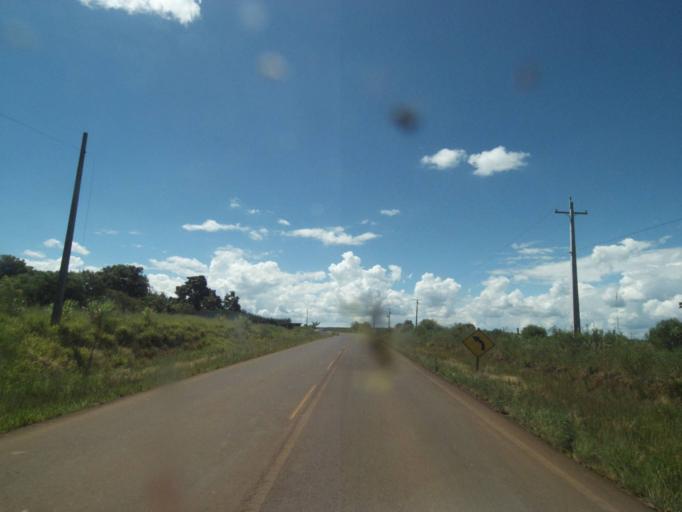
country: BR
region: Parana
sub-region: Pinhao
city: Pinhao
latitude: -25.8156
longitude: -52.0430
